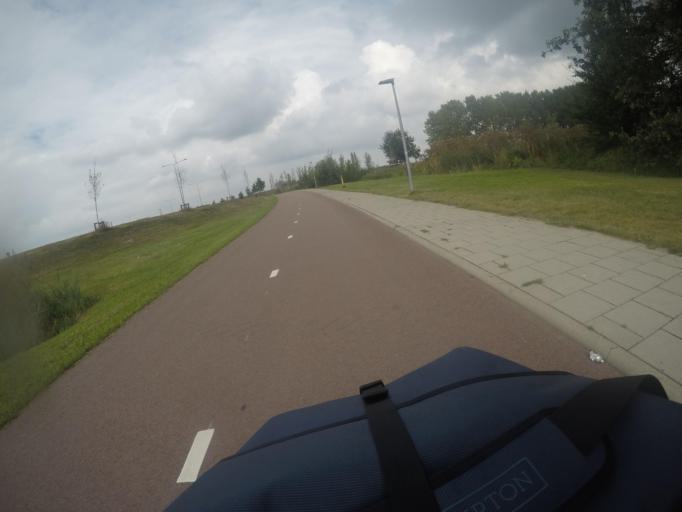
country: NL
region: Flevoland
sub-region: Gemeente Almere
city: Almere Stad
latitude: 52.3520
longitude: 5.2178
